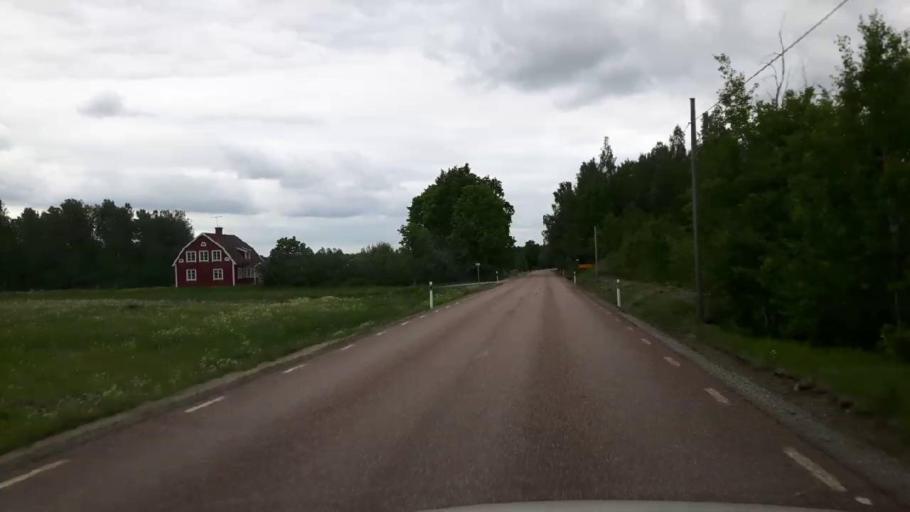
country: SE
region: Vaestmanland
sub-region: Kopings Kommun
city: Kolsva
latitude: 59.6890
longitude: 15.7744
